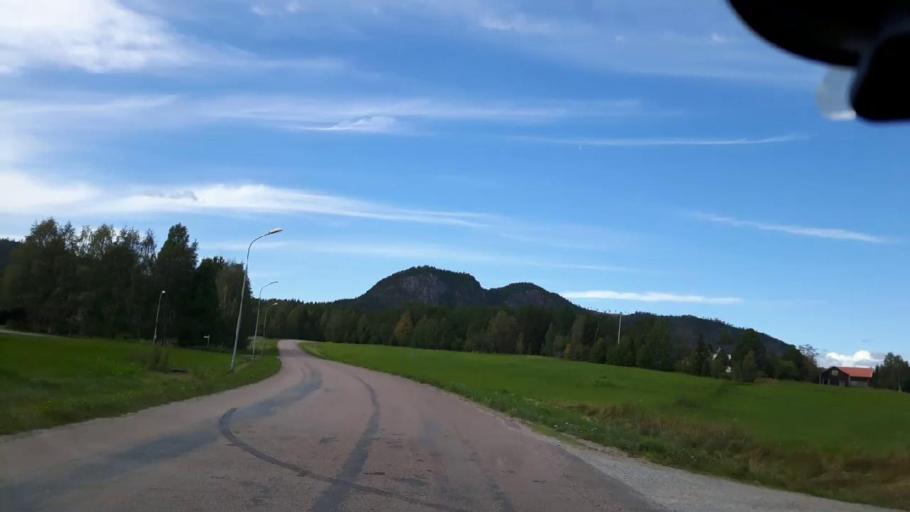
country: SE
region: Jaemtland
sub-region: Ragunda Kommun
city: Hammarstrand
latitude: 63.1156
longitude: 16.3467
